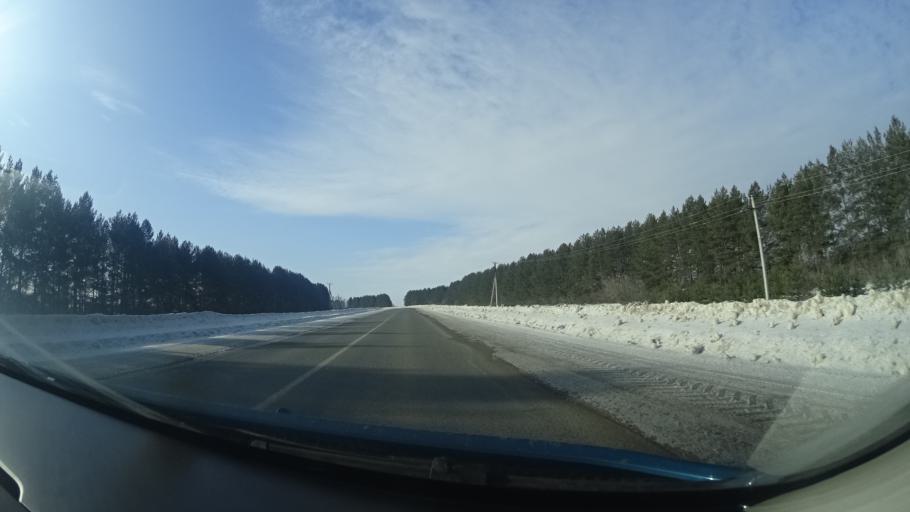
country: RU
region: Perm
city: Kuyeda
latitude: 56.4829
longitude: 55.5949
